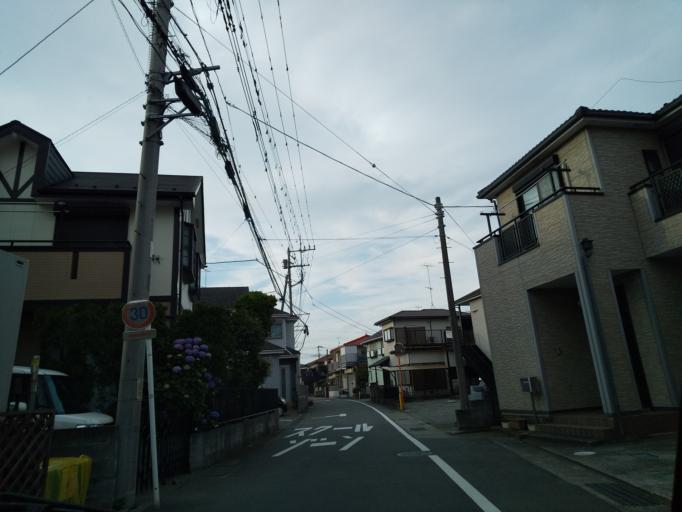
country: JP
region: Kanagawa
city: Zama
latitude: 35.5022
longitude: 139.3629
